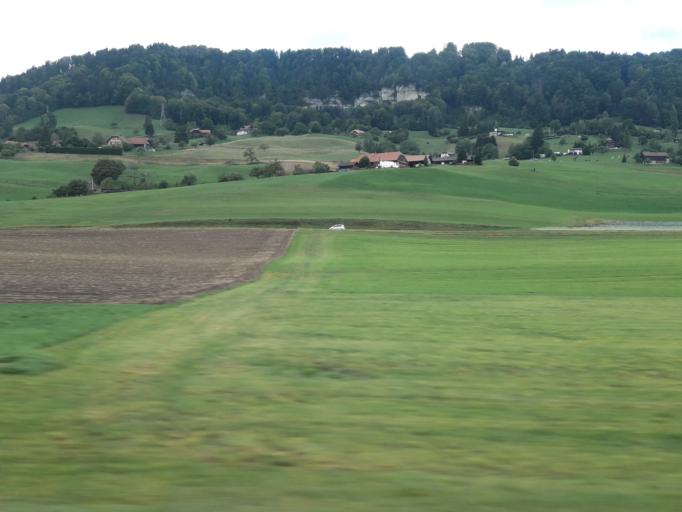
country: CH
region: Bern
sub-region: Bern-Mittelland District
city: Toffen
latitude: 46.8449
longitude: 7.4992
